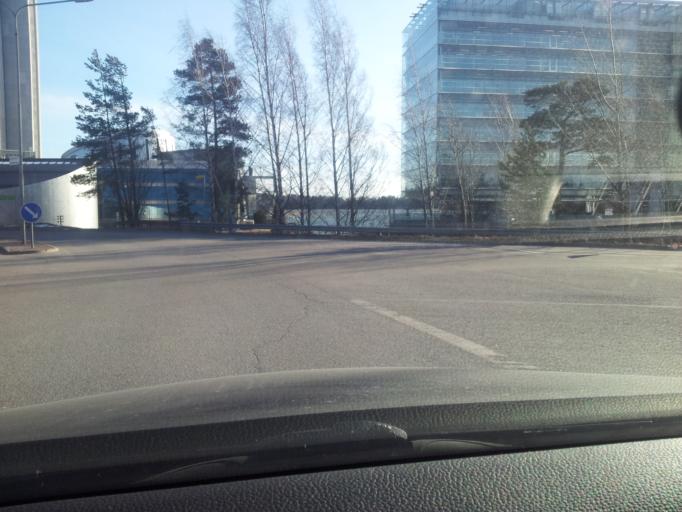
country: FI
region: Uusimaa
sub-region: Helsinki
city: Otaniemi
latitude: 60.1733
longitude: 24.8276
